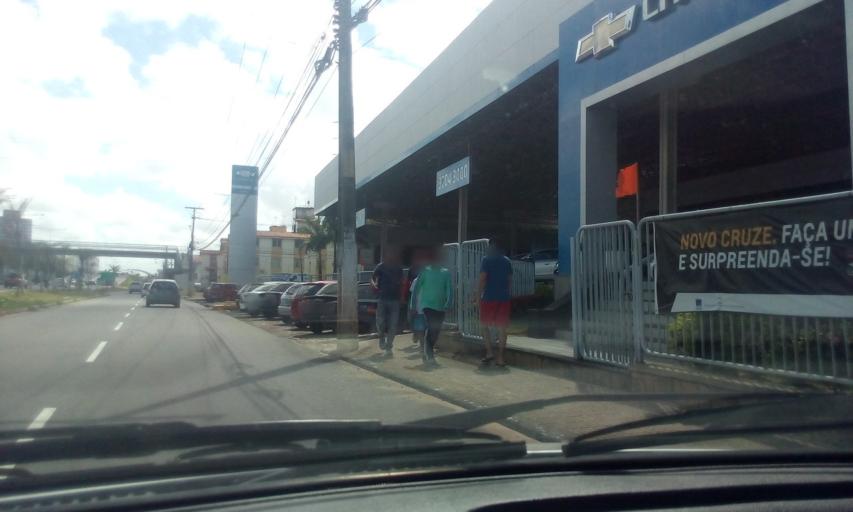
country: BR
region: Rio Grande do Norte
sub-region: Natal
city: Natal
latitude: -5.8545
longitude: -35.2116
